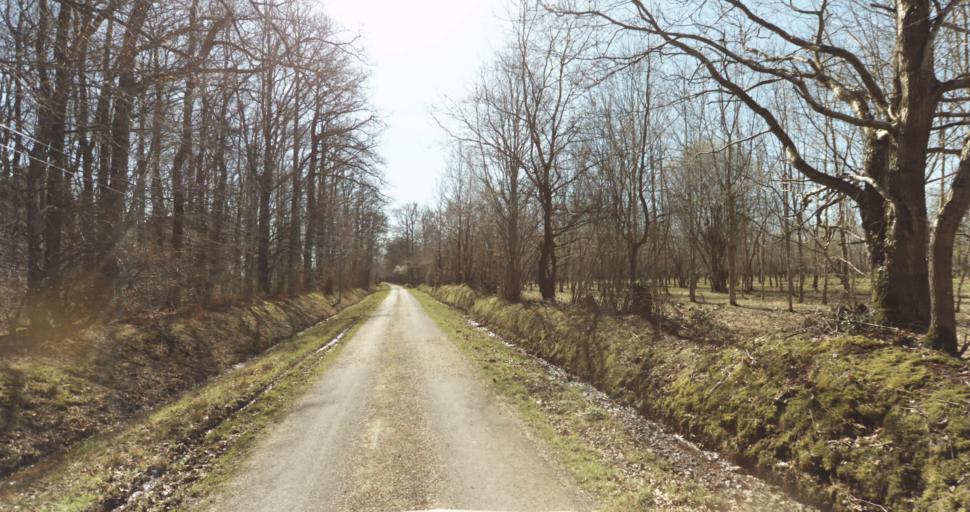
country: FR
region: Lower Normandy
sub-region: Departement du Calvados
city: Livarot
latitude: 48.9586
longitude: 0.0842
